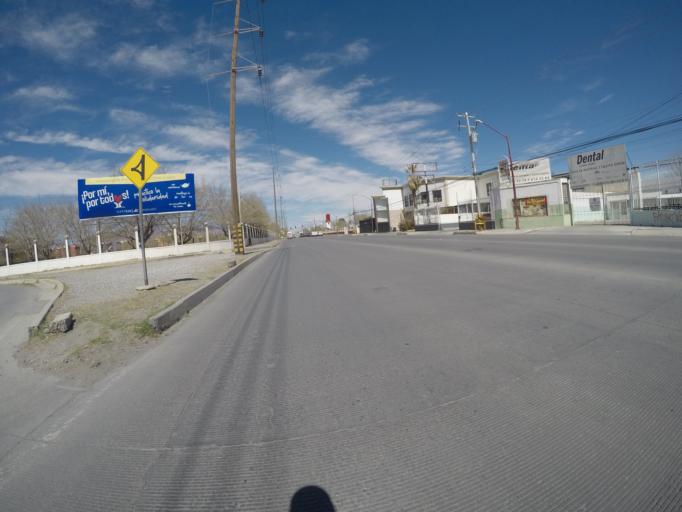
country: MX
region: Chihuahua
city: Ciudad Juarez
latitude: 31.7474
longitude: -106.4412
